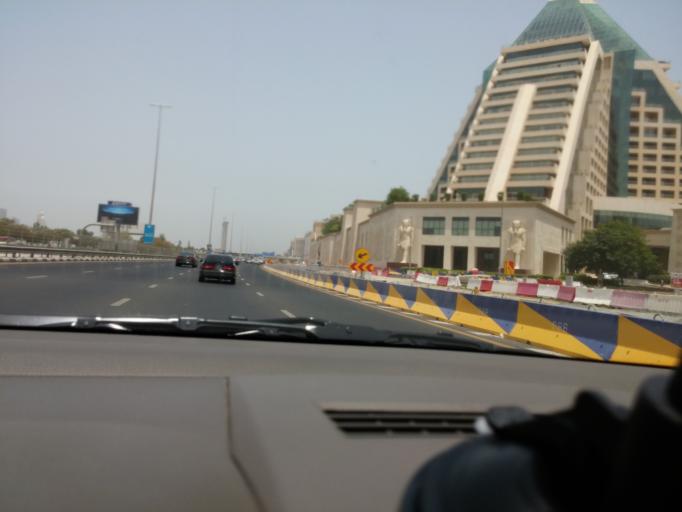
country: AE
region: Ash Shariqah
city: Sharjah
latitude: 25.2263
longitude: 55.3216
